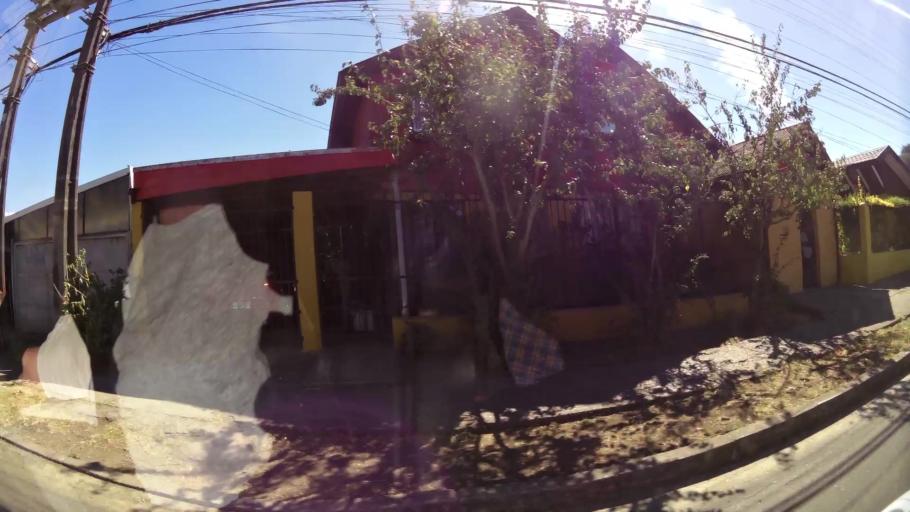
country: CL
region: Biobio
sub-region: Provincia de Concepcion
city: Penco
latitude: -36.7460
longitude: -72.9953
